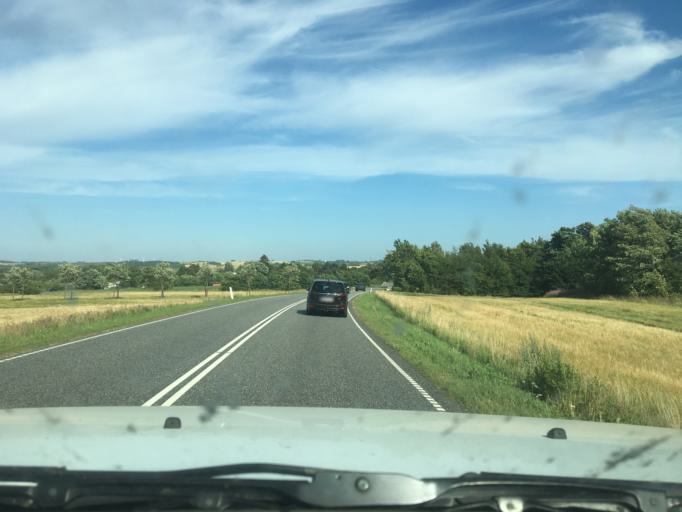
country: DK
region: Central Jutland
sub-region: Favrskov Kommune
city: Ulstrup
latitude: 56.4957
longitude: 9.8363
